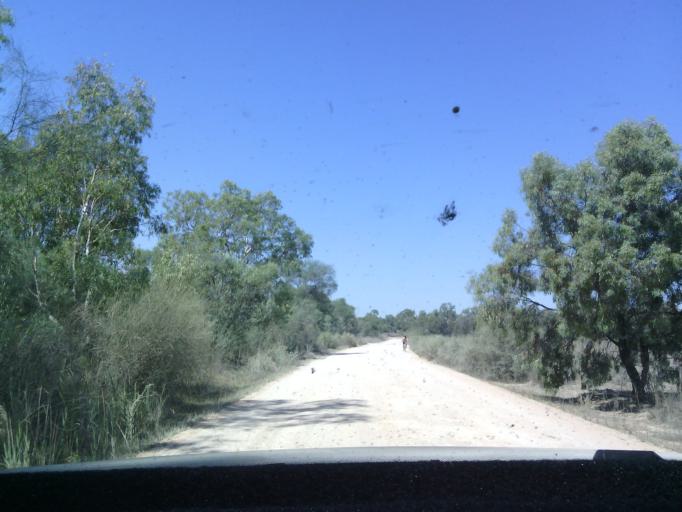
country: AU
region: South Australia
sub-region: Renmark Paringa
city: Renmark
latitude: -34.2162
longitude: 140.7382
